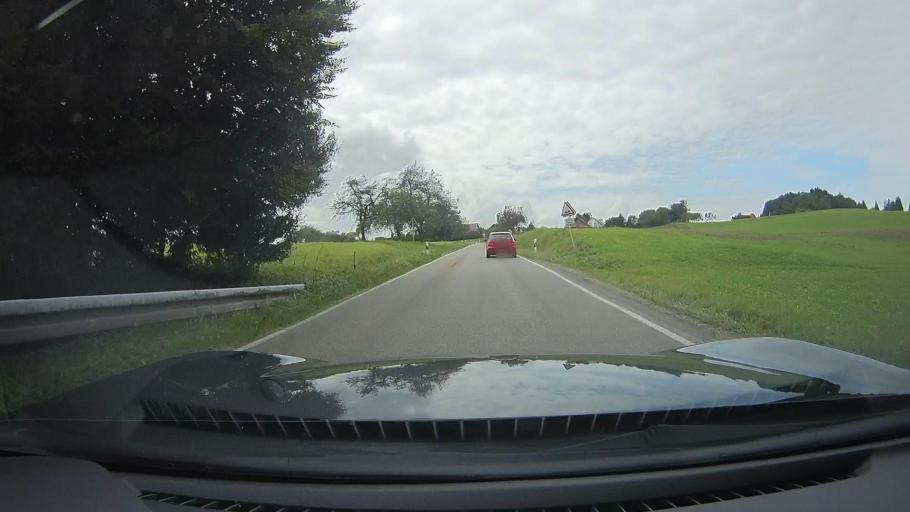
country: DE
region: Baden-Wuerttemberg
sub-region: Regierungsbezirk Stuttgart
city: Althutte
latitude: 48.9332
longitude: 9.5660
